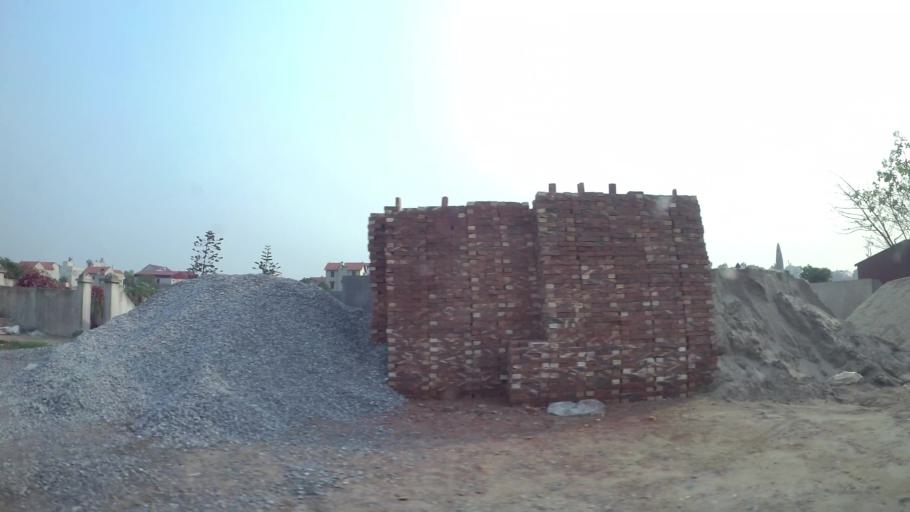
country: VN
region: Ha Noi
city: Thuong Tin
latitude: 20.8684
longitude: 105.8718
